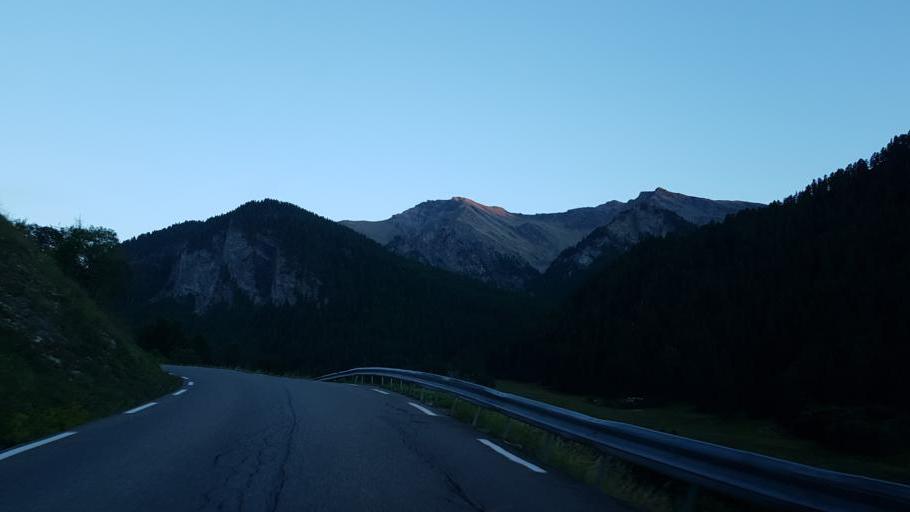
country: IT
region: Piedmont
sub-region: Provincia di Cuneo
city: Pontechianale
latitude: 44.7061
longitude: 6.8528
